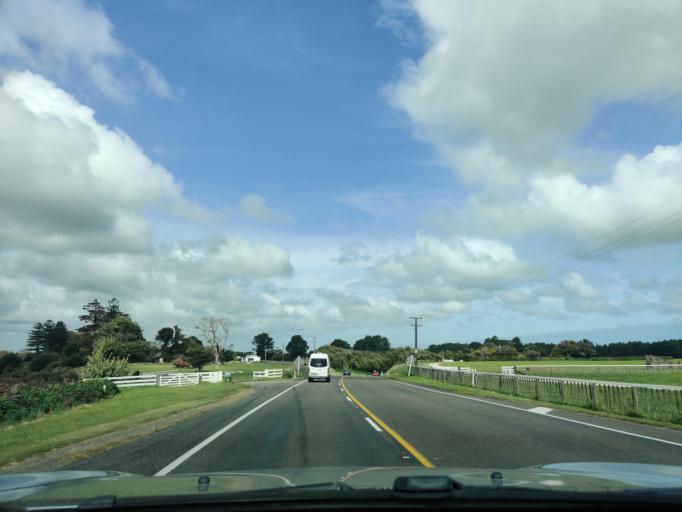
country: NZ
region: Manawatu-Wanganui
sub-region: Wanganui District
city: Wanganui
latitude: -39.8182
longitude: 174.8332
